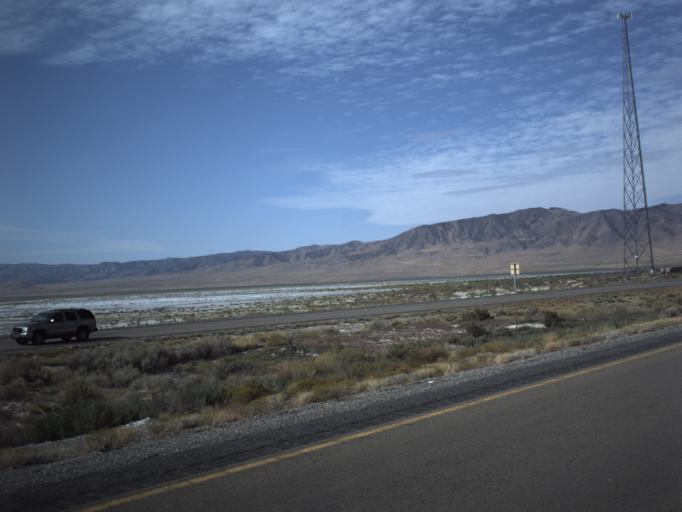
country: US
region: Utah
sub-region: Tooele County
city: Grantsville
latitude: 40.7578
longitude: -112.7686
